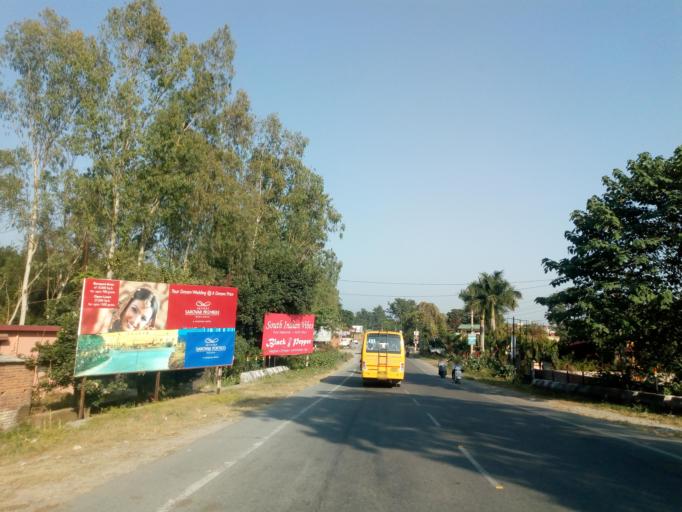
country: IN
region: Uttarakhand
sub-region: Dehradun
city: Dehradun
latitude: 30.3444
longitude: 77.9250
